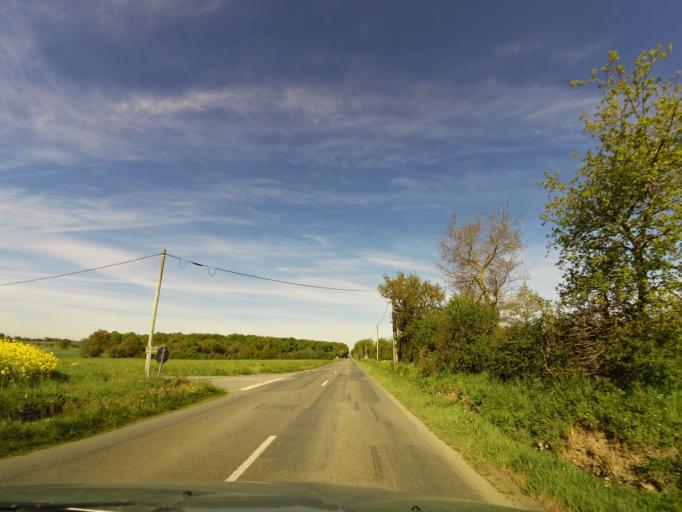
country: FR
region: Brittany
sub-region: Departement d'Ille-et-Vilaine
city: Pance
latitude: 47.8722
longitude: -1.6201
